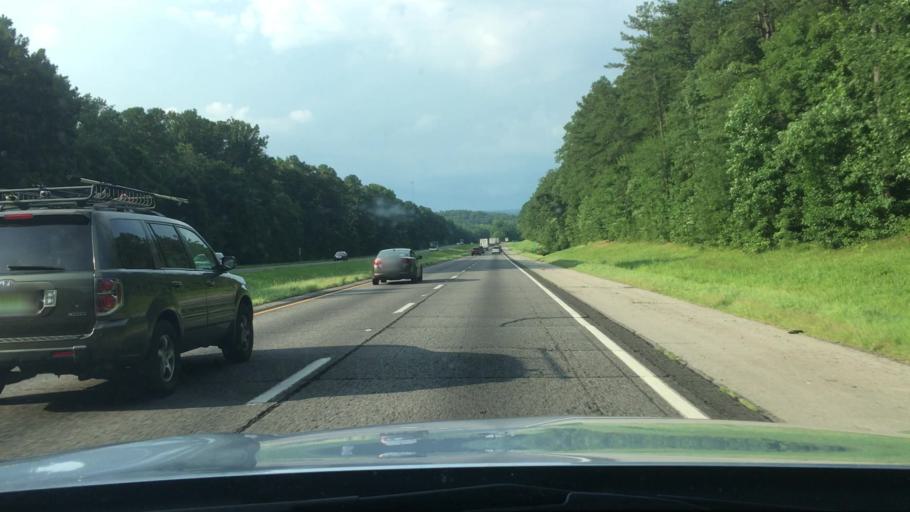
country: US
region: Alabama
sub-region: Saint Clair County
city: Springville
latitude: 33.7456
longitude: -86.4858
